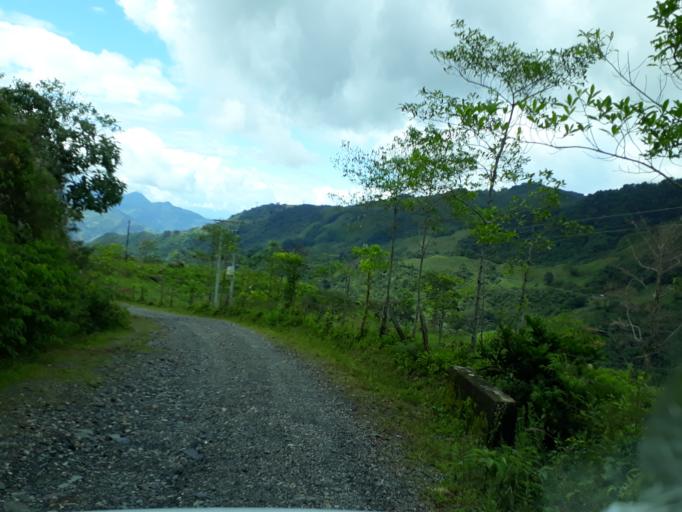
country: CO
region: Cundinamarca
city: Gachala
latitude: 4.7109
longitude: -73.3647
